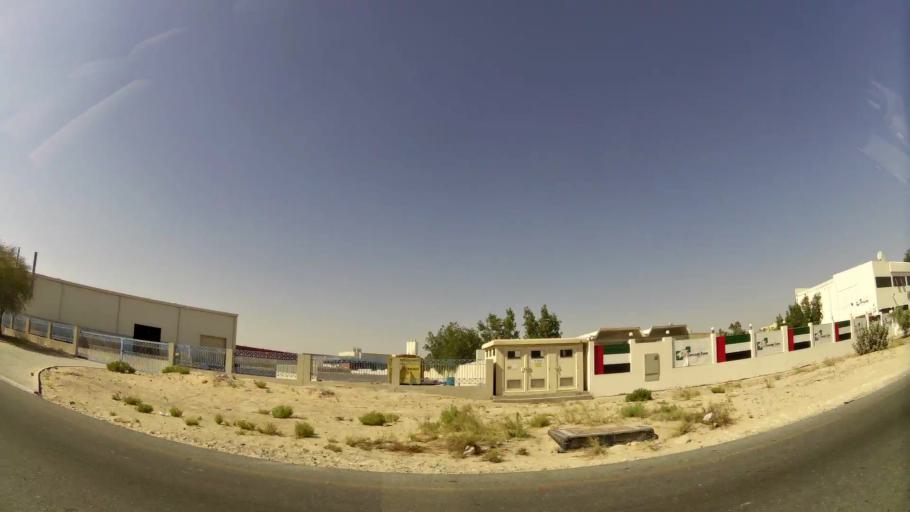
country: AE
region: Dubai
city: Dubai
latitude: 24.9404
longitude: 55.0652
